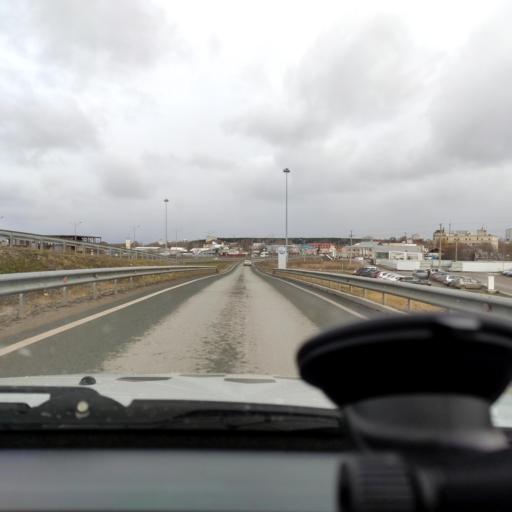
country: RU
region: Perm
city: Kondratovo
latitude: 57.9538
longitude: 56.1238
